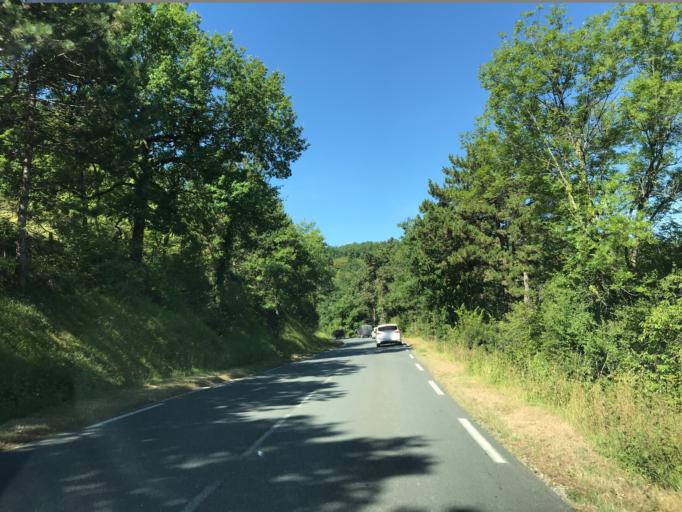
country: FR
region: Limousin
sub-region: Departement de la Correze
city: Larche
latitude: 45.1013
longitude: 1.3907
